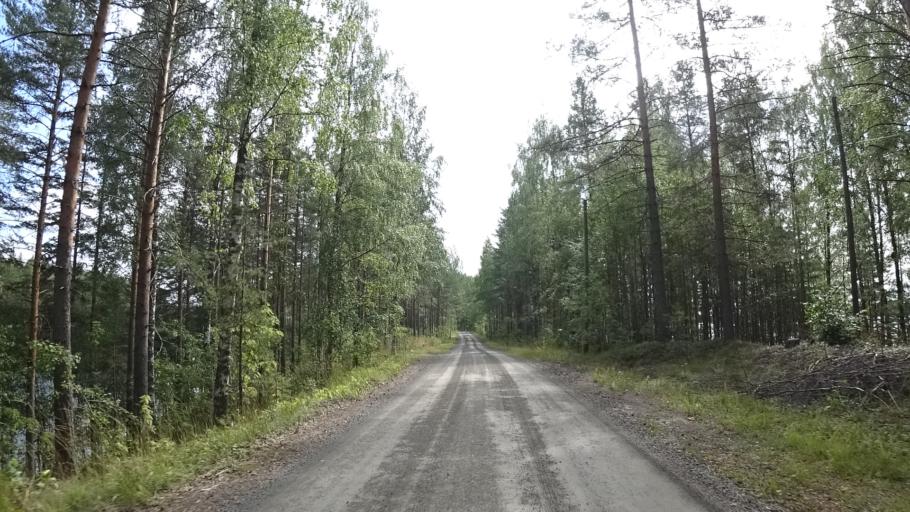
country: FI
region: North Karelia
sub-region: Joensuu
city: Pyhaeselkae
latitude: 62.3791
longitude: 29.8094
